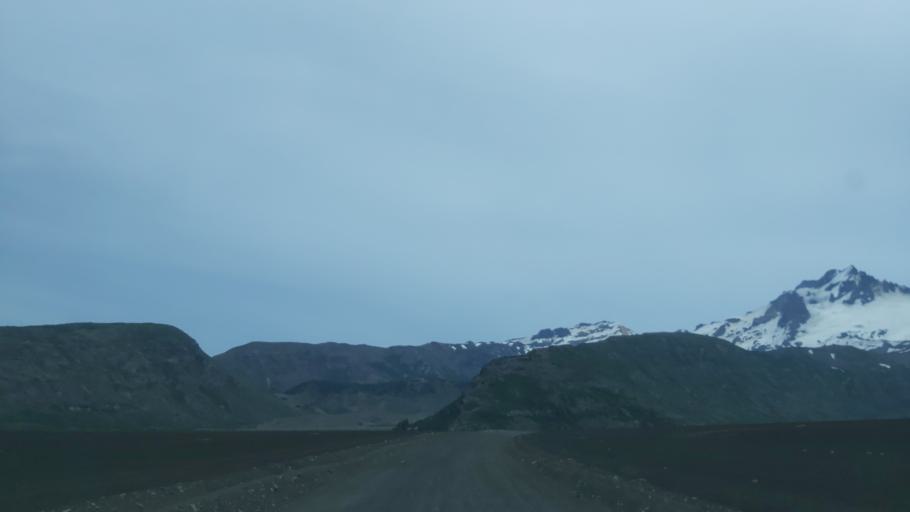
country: AR
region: Neuquen
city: Andacollo
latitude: -37.4592
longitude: -71.3042
